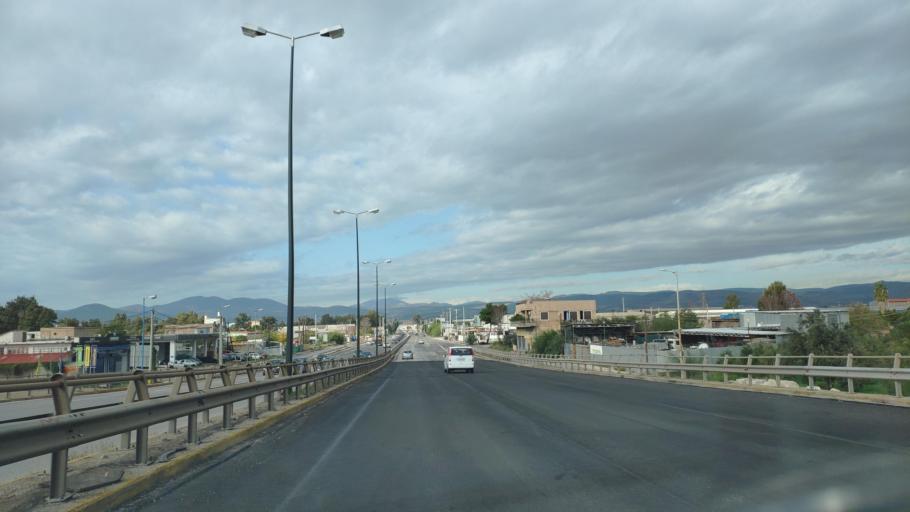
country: GR
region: Attica
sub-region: Nomarchia Dytikis Attikis
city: Aspropyrgos
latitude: 38.0437
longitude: 23.5834
